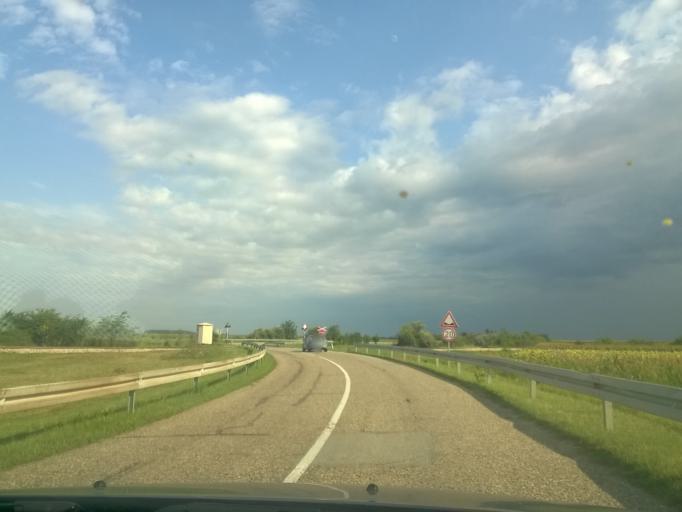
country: RS
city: Uzdin
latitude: 45.1825
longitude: 20.6185
